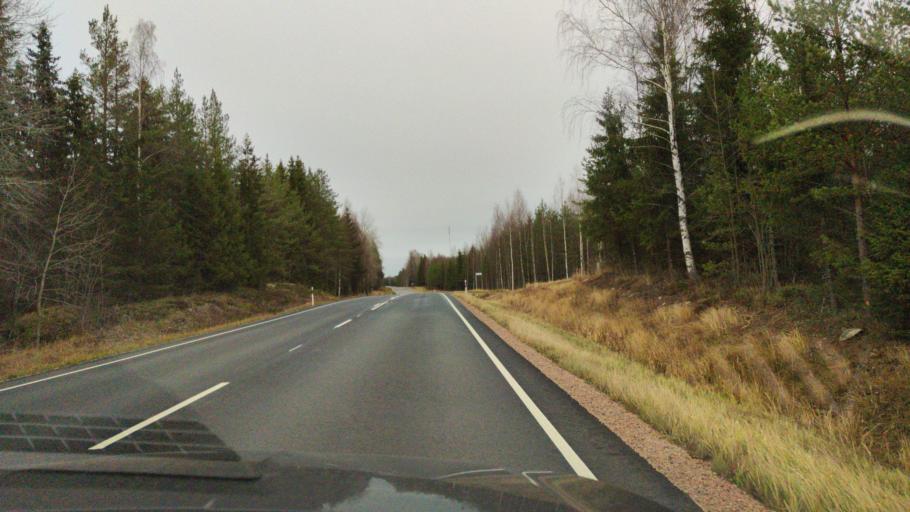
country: FI
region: Varsinais-Suomi
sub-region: Loimaa
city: Aura
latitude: 60.7142
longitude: 22.4443
